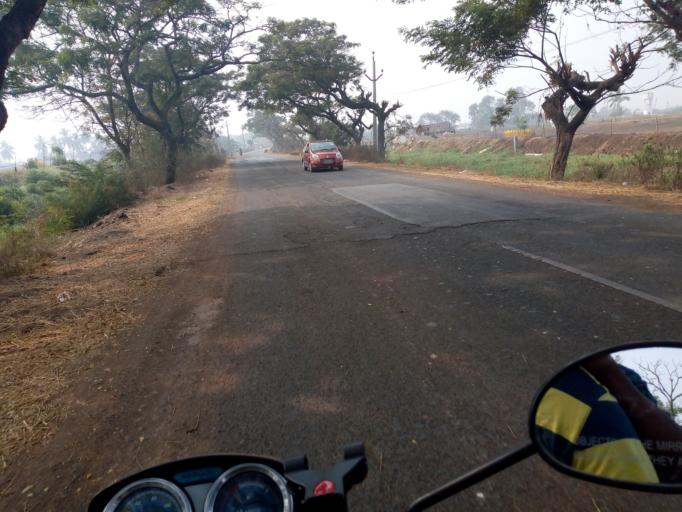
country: IN
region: Andhra Pradesh
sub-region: West Godavari
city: Tadepallegudem
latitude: 16.7480
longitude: 81.4211
